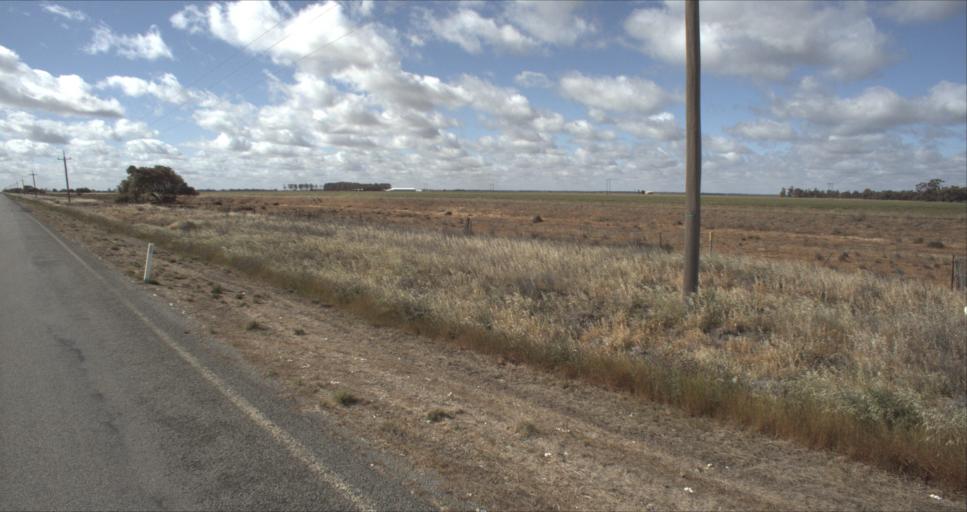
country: AU
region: New South Wales
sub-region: Leeton
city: Leeton
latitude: -34.5240
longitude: 146.2031
